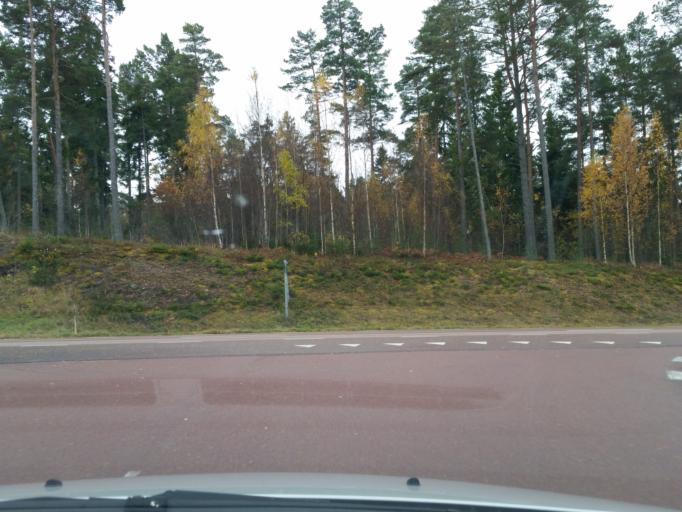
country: AX
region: Alands landsbygd
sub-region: Lemland
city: Lemland
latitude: 60.0674
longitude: 20.0729
